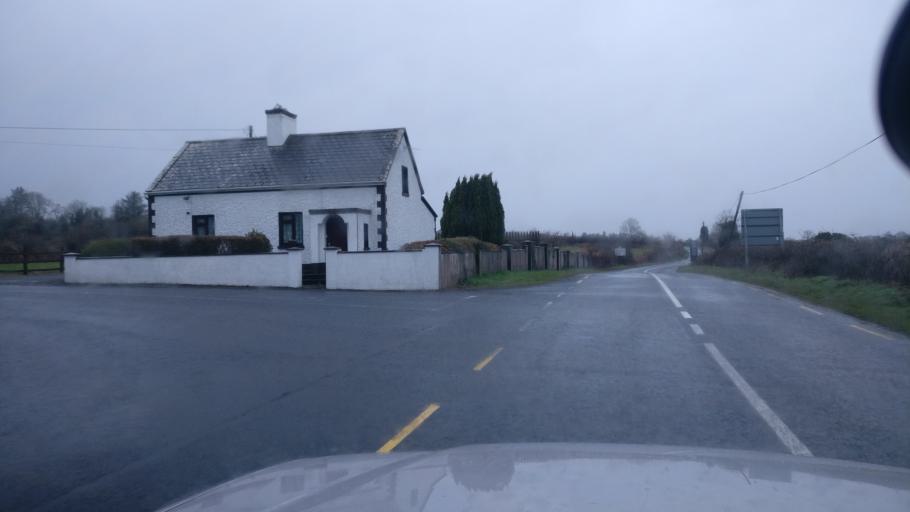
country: IE
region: Connaught
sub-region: County Galway
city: Loughrea
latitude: 53.0966
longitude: -8.4265
